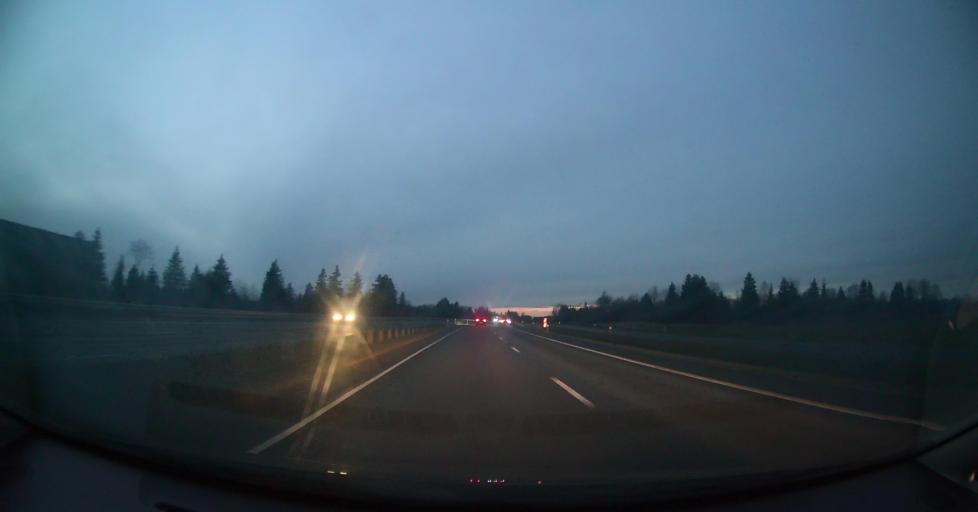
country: EE
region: Harju
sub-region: Rae vald
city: Vaida
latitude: 59.1841
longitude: 25.0803
